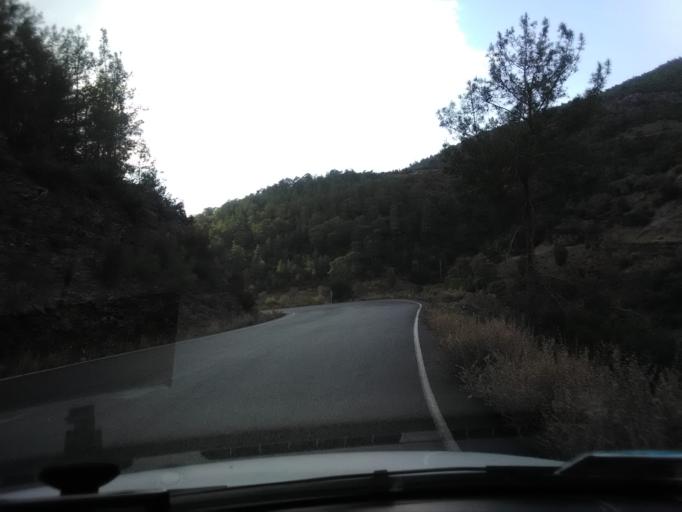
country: TR
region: Antalya
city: Gazipasa
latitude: 36.2932
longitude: 32.3784
